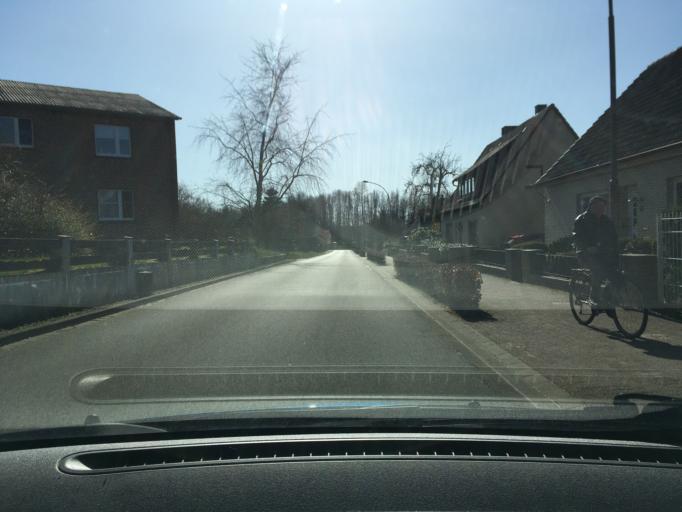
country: DE
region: Lower Saxony
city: Ebstorf
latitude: 53.0208
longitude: 10.4061
